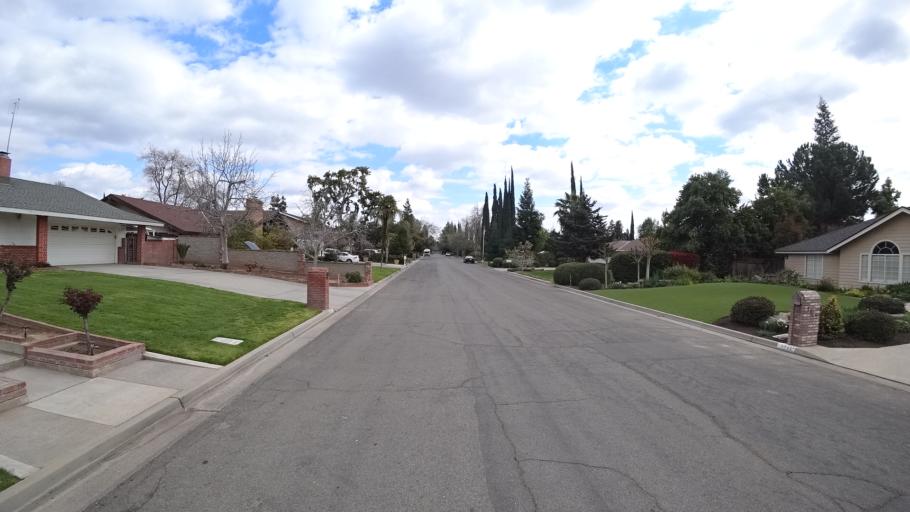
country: US
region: California
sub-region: Fresno County
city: Fresno
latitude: 36.8250
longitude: -119.8441
